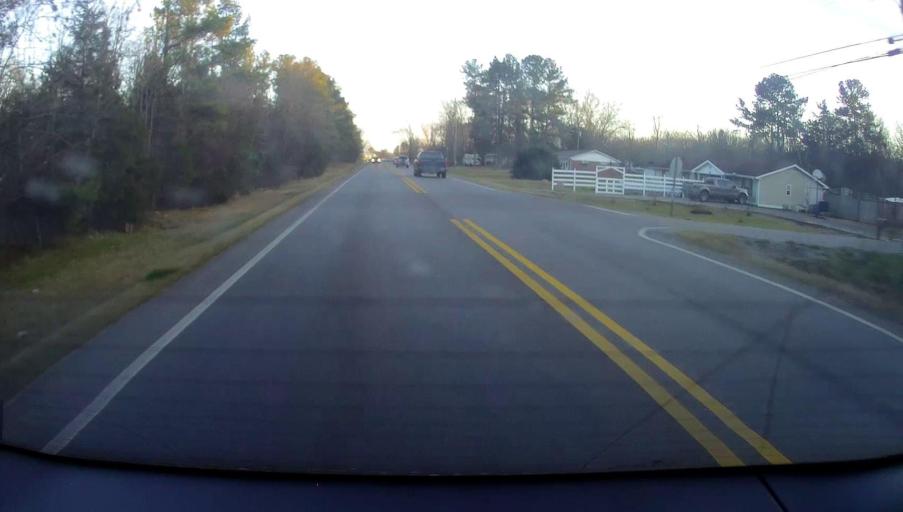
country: US
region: Alabama
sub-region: Etowah County
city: Attalla
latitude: 34.0089
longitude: -86.1196
